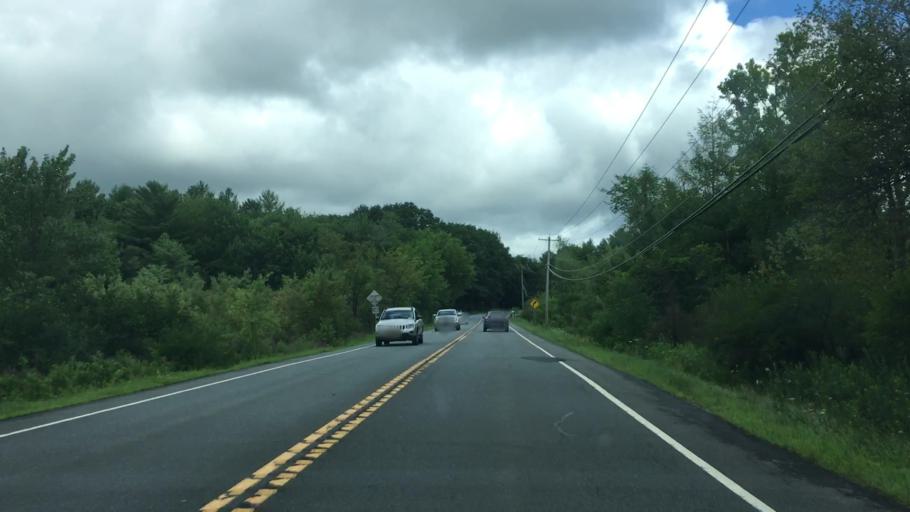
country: US
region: New York
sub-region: Rensselaer County
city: Poestenkill
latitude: 42.8265
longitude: -73.4952
